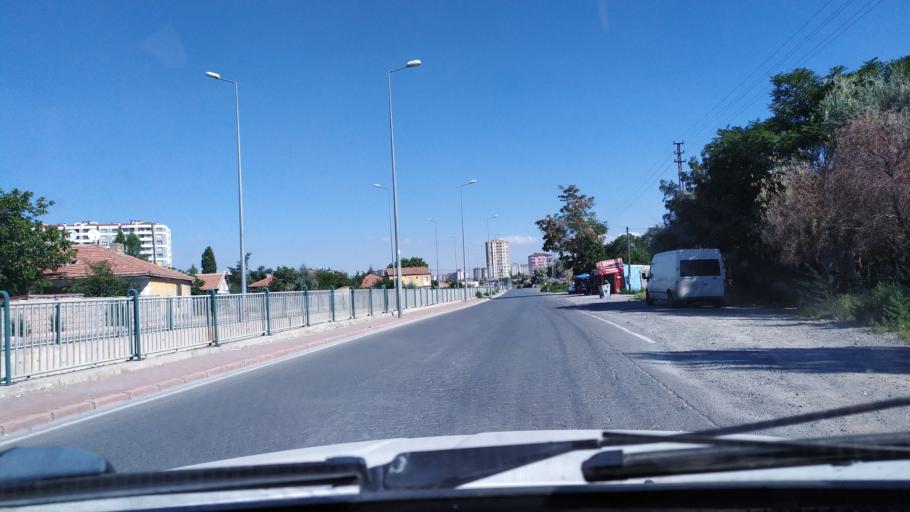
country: TR
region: Kayseri
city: Talas
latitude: 38.7228
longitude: 35.5504
